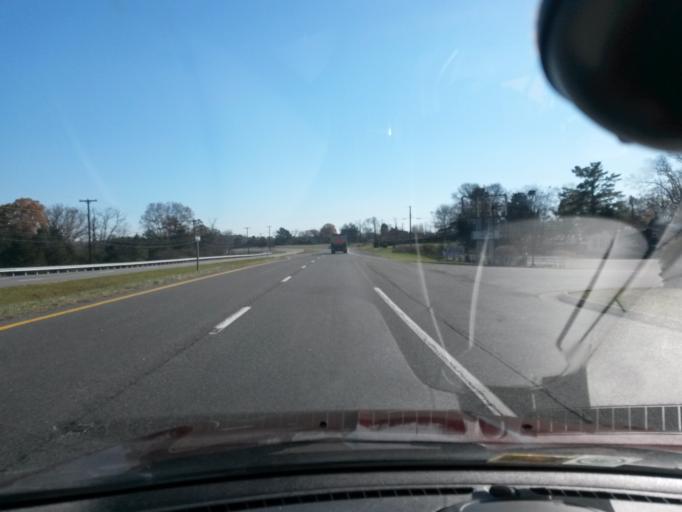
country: US
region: Virginia
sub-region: City of Bedford
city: Bedford
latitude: 37.3220
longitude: -79.4929
